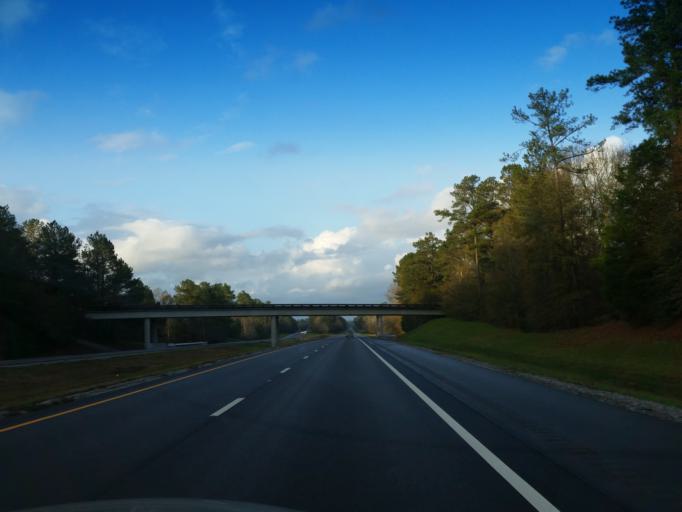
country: US
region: Mississippi
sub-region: Jones County
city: Sharon
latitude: 31.8360
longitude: -89.0498
